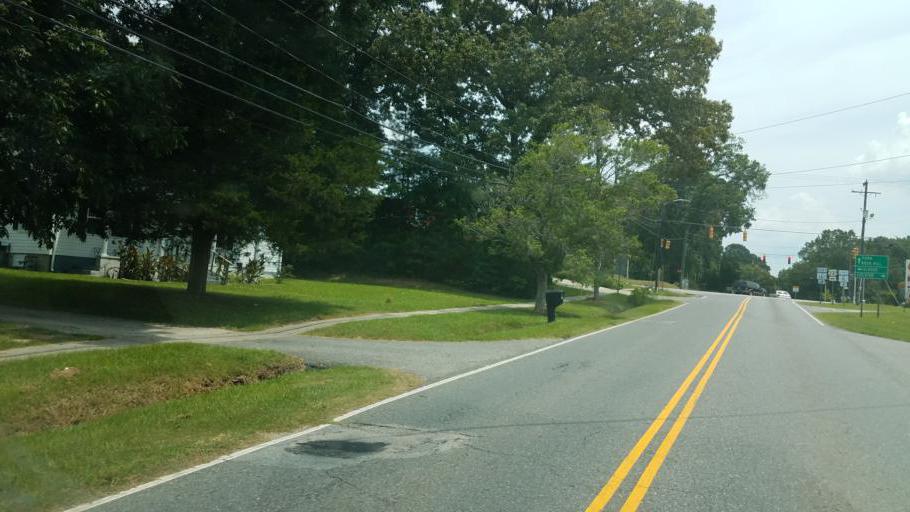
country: US
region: South Carolina
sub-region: York County
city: York
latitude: 34.9982
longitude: -81.2522
